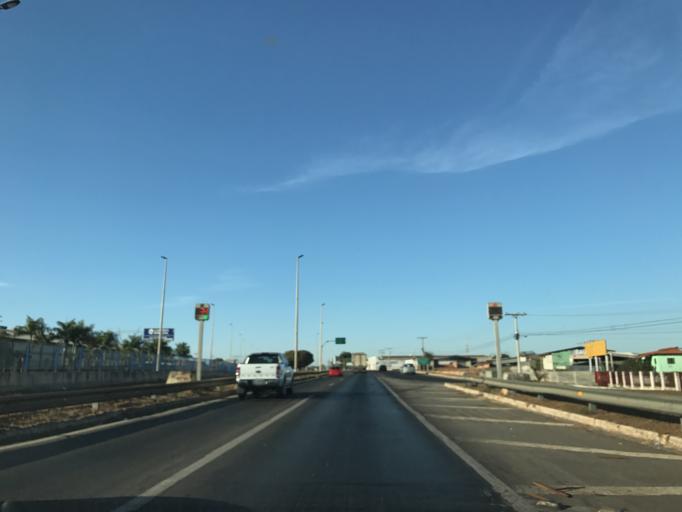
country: BR
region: Goias
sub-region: Aparecida De Goiania
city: Aparecida de Goiania
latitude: -16.8111
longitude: -49.2398
